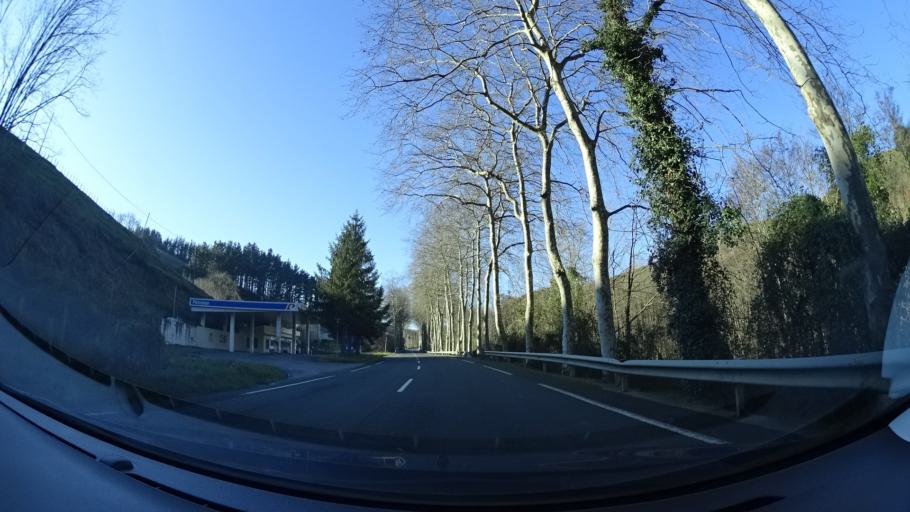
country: ES
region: Basque Country
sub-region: Provincia de Guipuzcoa
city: Zumaia
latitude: 43.2726
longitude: -2.2776
